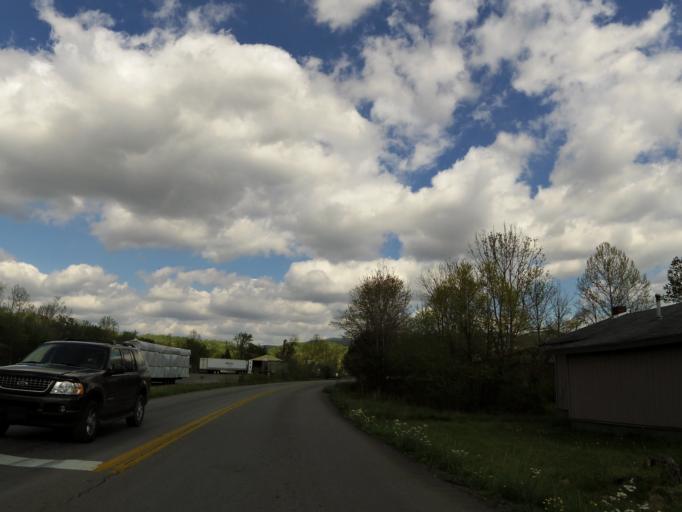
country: US
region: Kentucky
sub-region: Bell County
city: Middlesboro
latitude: 36.6236
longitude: -83.7162
